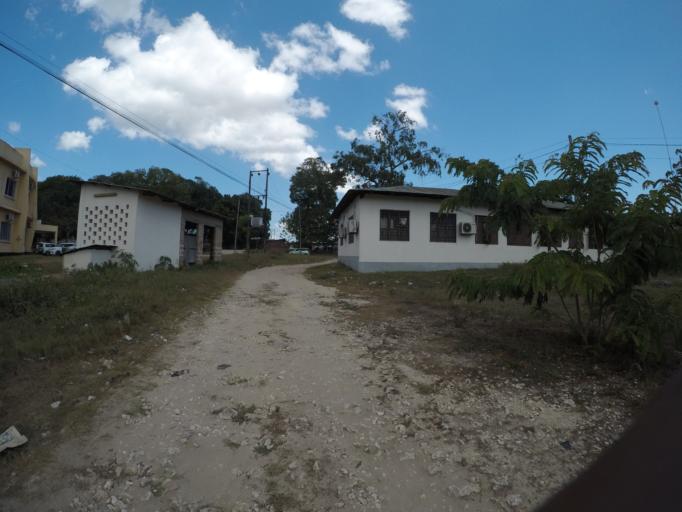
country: TZ
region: Zanzibar Urban/West
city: Zanzibar
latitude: -6.1474
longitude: 39.2100
